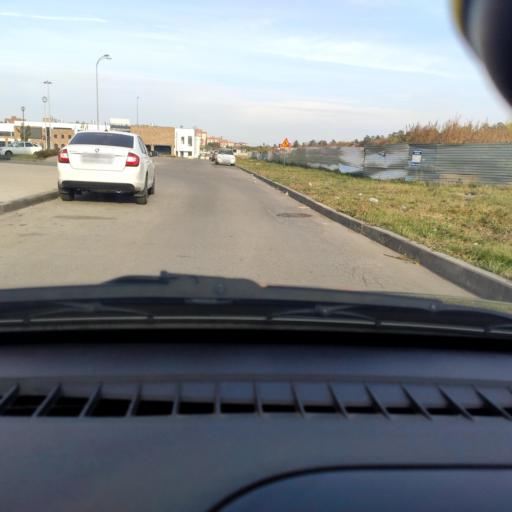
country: RU
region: Samara
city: Tol'yatti
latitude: 53.5294
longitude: 49.3433
